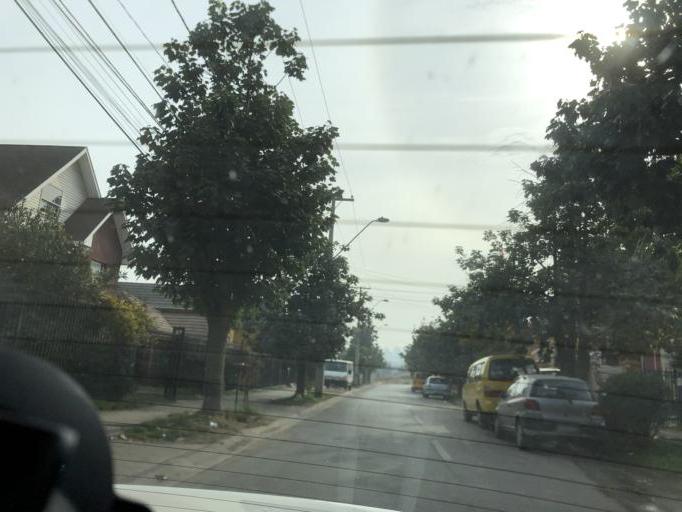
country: CL
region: Santiago Metropolitan
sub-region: Provincia de Cordillera
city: Puente Alto
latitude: -33.5635
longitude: -70.5473
